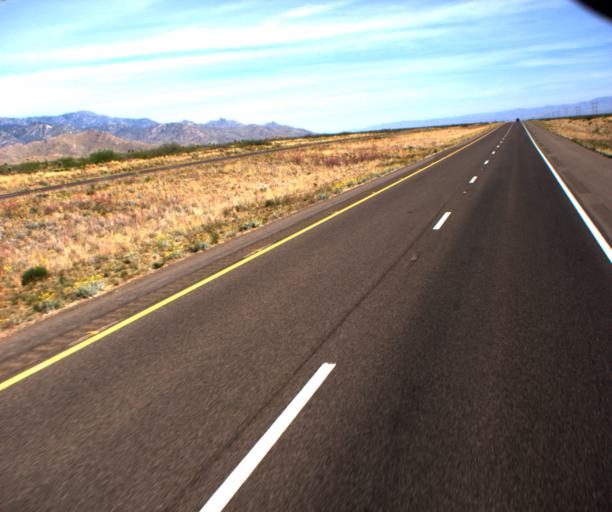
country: US
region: Arizona
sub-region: Graham County
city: Swift Trail Junction
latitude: 32.5460
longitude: -109.6767
